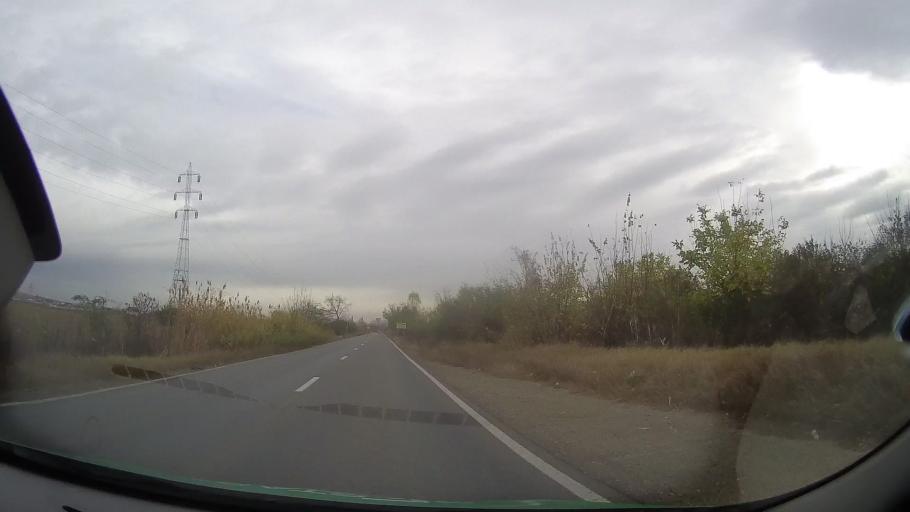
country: RO
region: Prahova
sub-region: Comuna Bucov
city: Bucov
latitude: 44.9509
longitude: 26.0935
